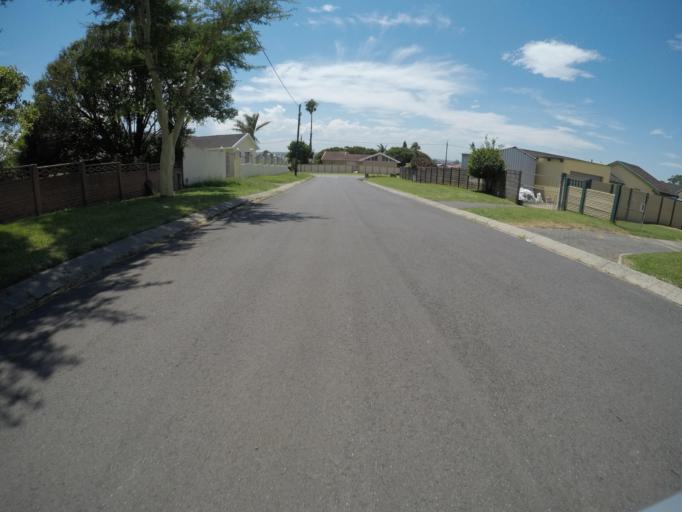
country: ZA
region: Eastern Cape
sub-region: Buffalo City Metropolitan Municipality
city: East London
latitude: -33.0327
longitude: 27.8507
